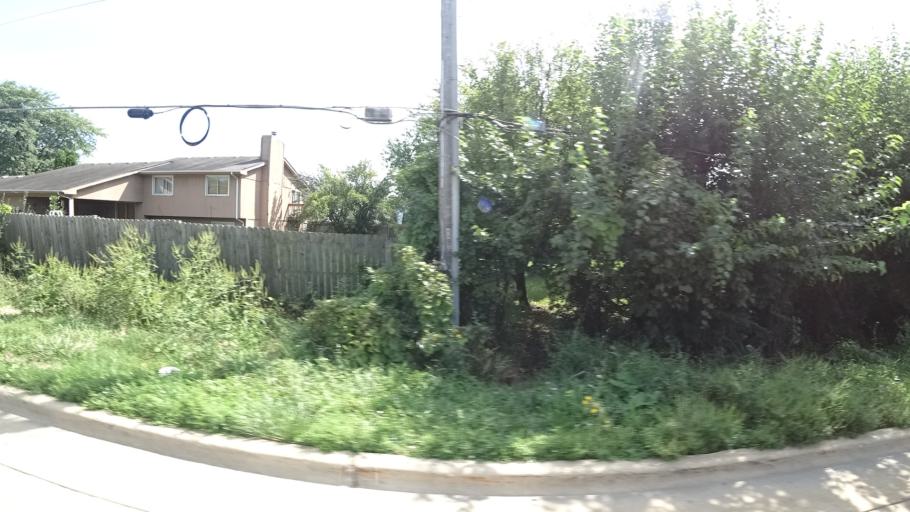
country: US
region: Illinois
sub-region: Will County
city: Frankfort Square
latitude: 41.5280
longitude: -87.7626
